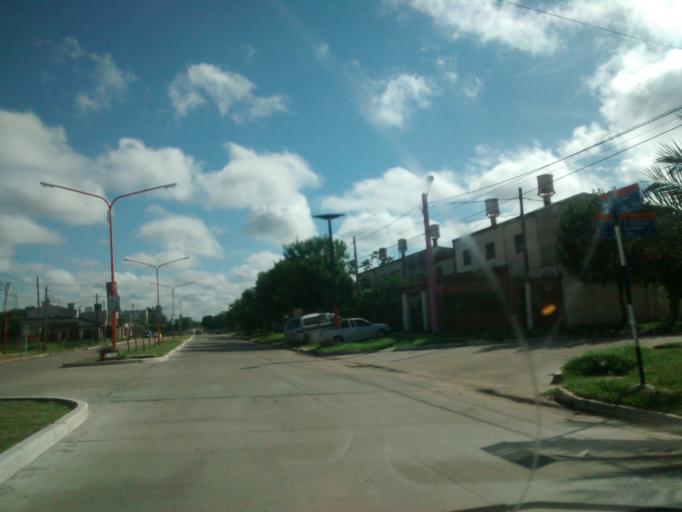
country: AR
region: Chaco
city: Resistencia
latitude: -27.4408
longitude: -58.9663
